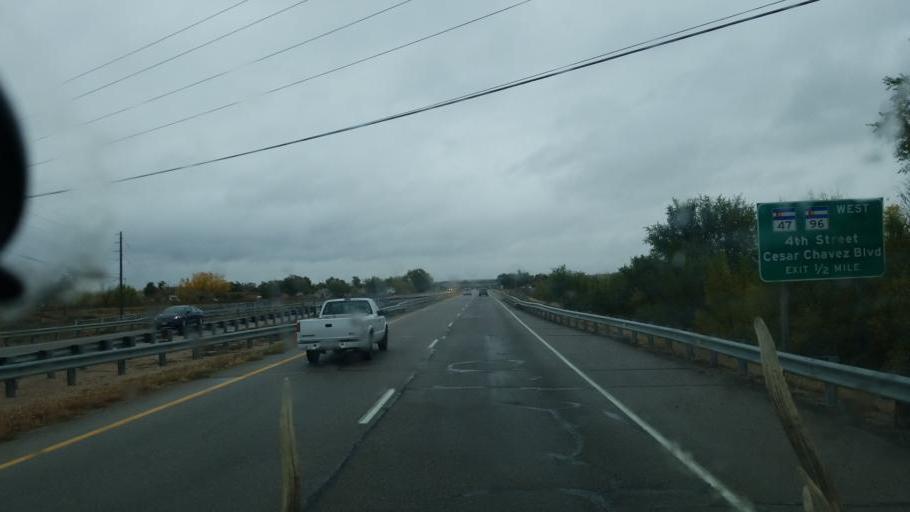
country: US
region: Colorado
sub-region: Pueblo County
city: Pueblo
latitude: 38.2807
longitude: -104.5689
